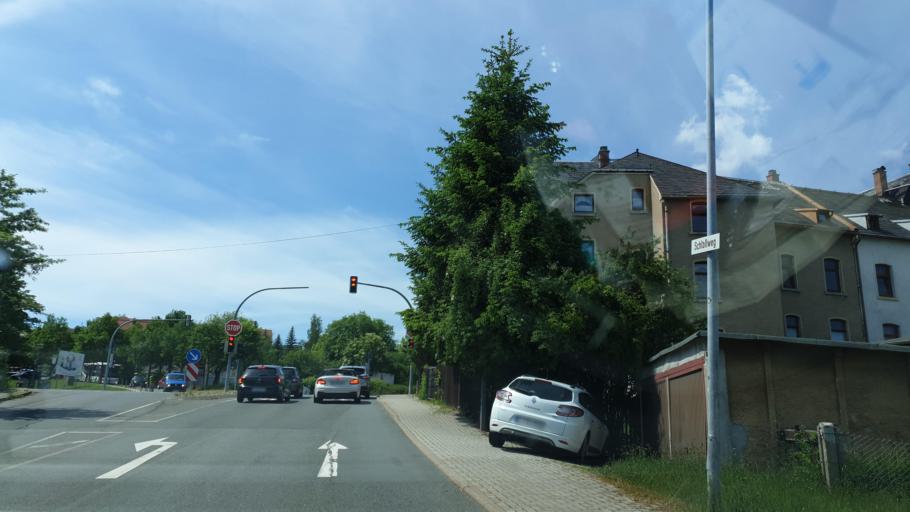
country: DE
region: Saxony
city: Auerbach
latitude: 50.5172
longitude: 12.3861
